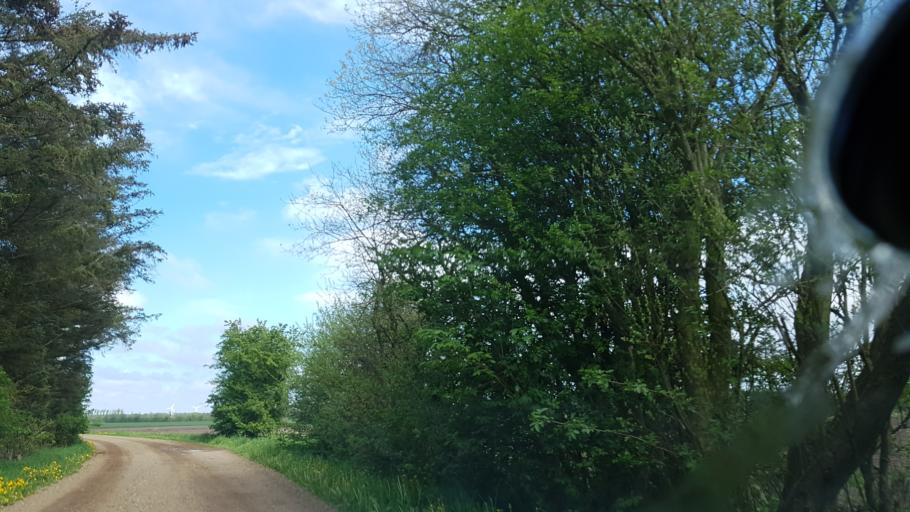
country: DK
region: South Denmark
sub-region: Tonder Kommune
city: Sherrebek
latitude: 55.0852
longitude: 8.8427
